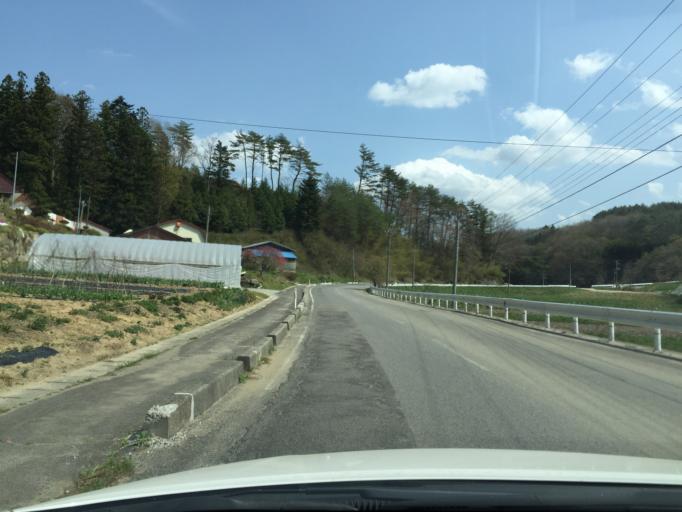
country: JP
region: Fukushima
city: Namie
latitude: 37.4014
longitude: 140.8007
